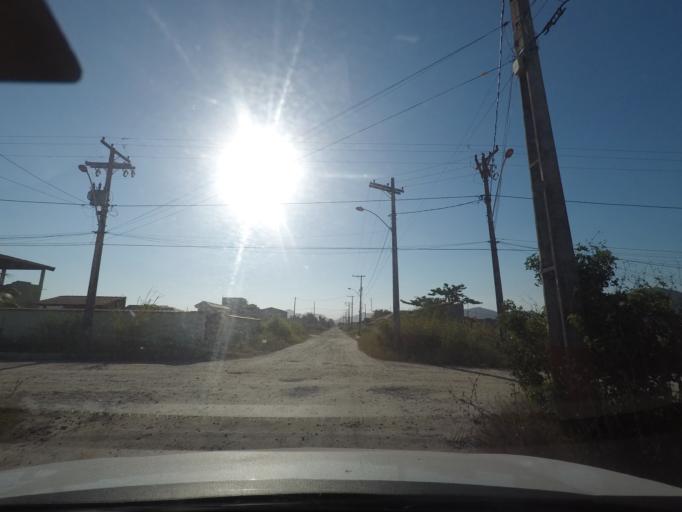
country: BR
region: Rio de Janeiro
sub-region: Marica
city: Marica
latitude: -22.9619
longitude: -42.9334
